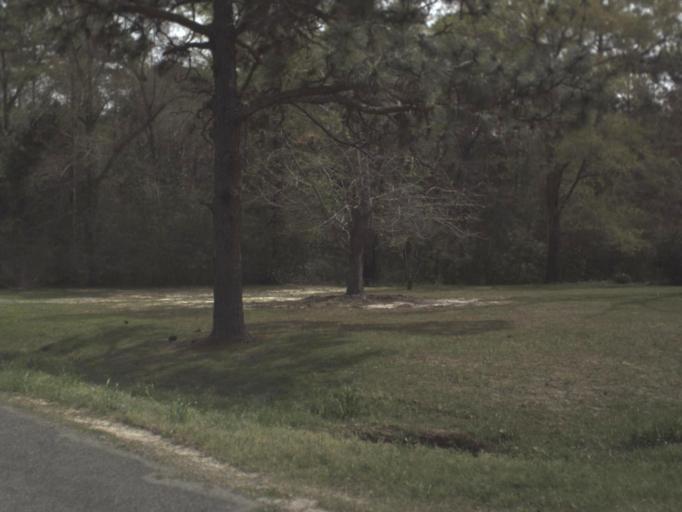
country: US
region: Alabama
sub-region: Geneva County
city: Geneva
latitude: 30.9540
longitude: -85.8848
